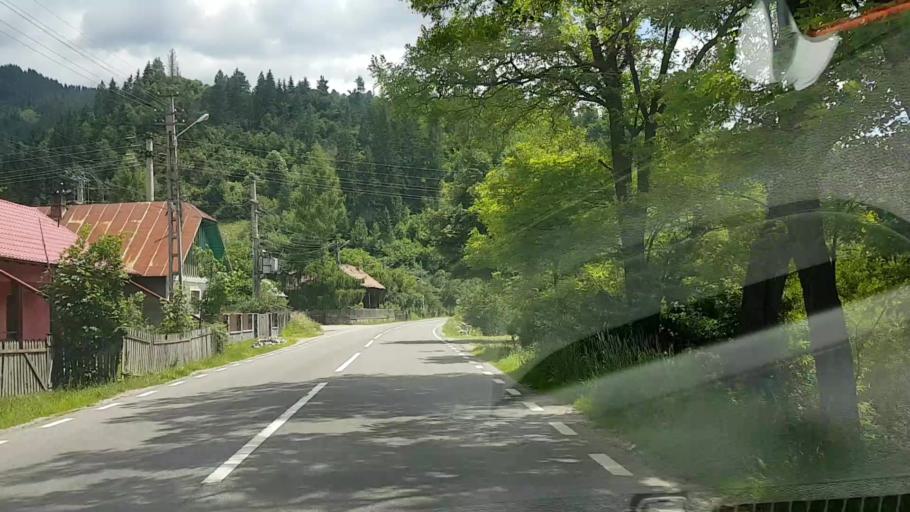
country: RO
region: Suceava
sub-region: Comuna Brosteni
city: Brosteni
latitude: 47.2546
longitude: 25.6938
